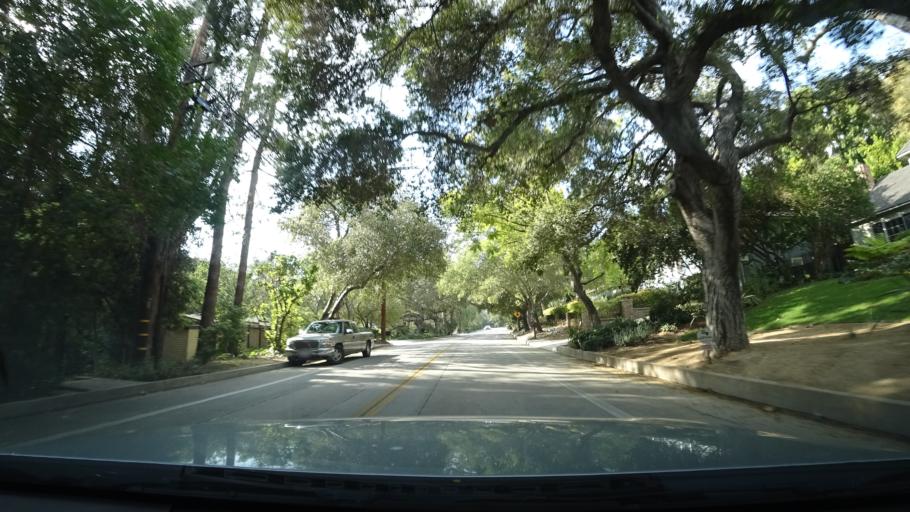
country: US
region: California
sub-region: Los Angeles County
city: South Pasadena
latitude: 34.1286
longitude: -118.1717
